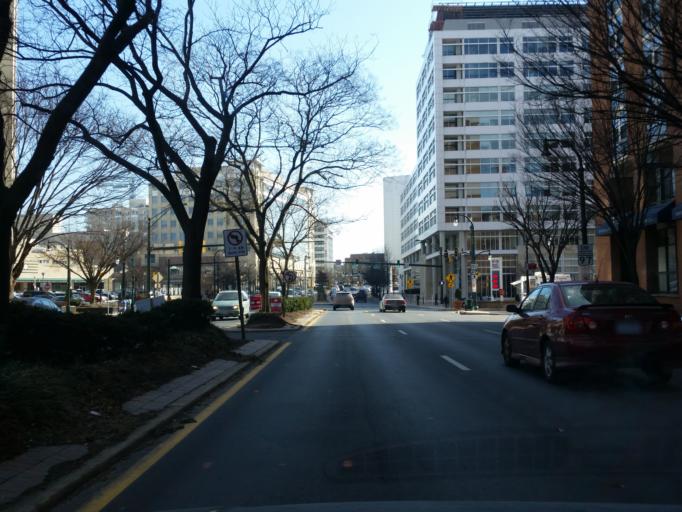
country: US
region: Maryland
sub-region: Montgomery County
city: Silver Spring
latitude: 38.9968
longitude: -77.0289
